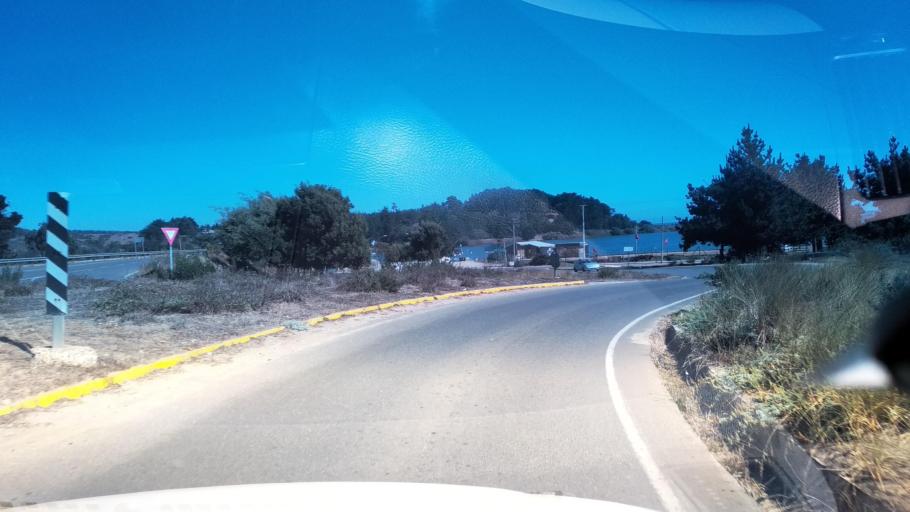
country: CL
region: O'Higgins
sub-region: Provincia de Colchagua
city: Santa Cruz
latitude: -34.4770
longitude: -72.0171
